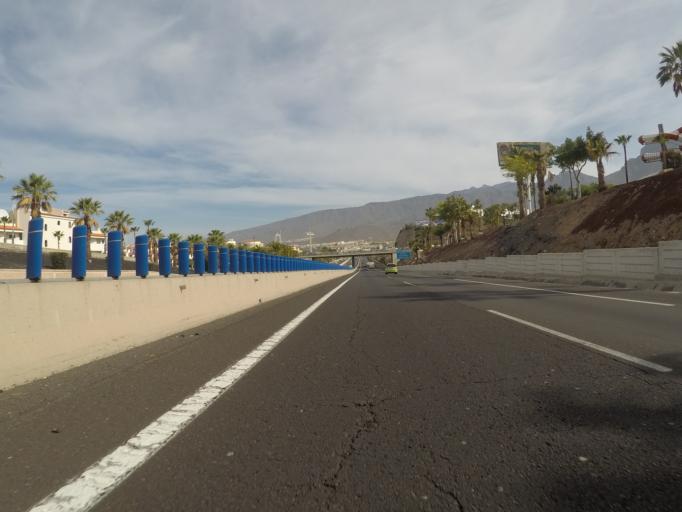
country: ES
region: Canary Islands
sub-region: Provincia de Santa Cruz de Tenerife
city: Playa de las Americas
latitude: 28.0797
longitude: -16.7295
